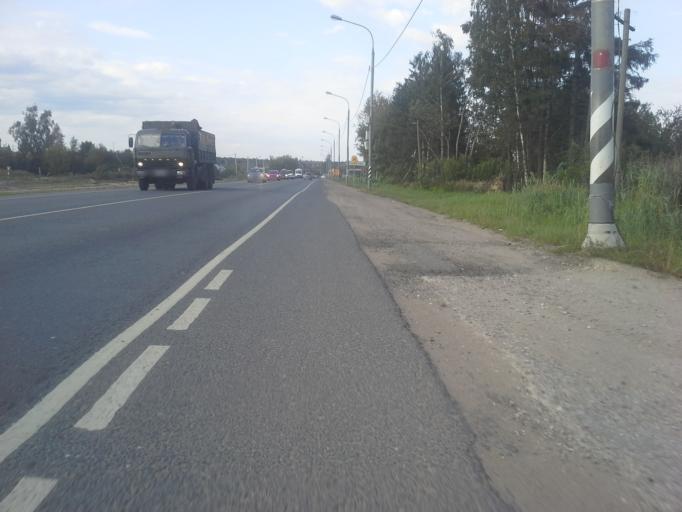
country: RU
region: Moskovskaya
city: Golitsyno
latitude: 55.5894
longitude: 37.0033
